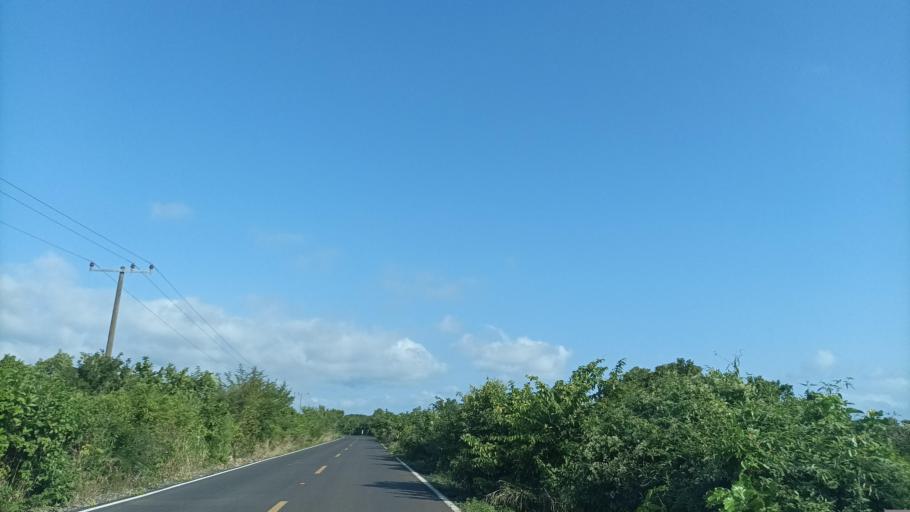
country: MX
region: Veracruz
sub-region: Chinameca
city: Chacalapa
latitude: 18.1452
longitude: -94.6535
